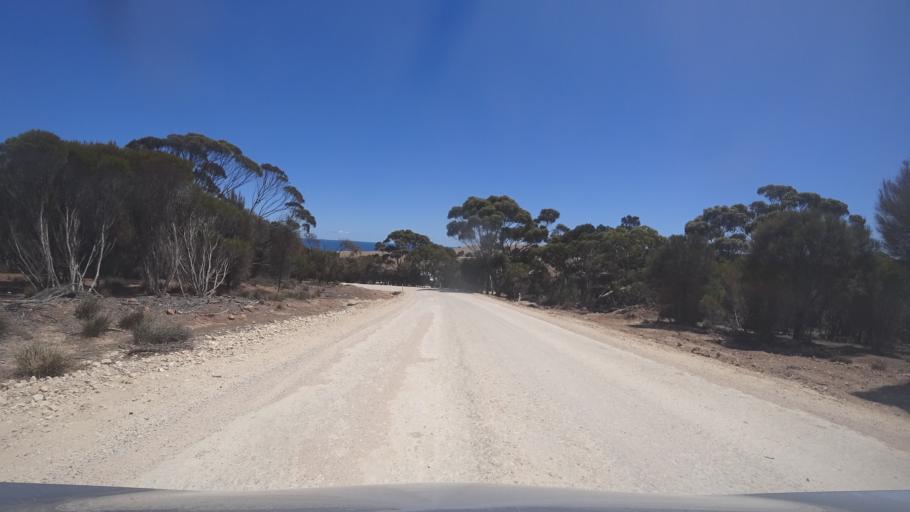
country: AU
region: South Australia
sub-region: Kangaroo Island
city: Kingscote
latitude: -35.6269
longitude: 137.2121
